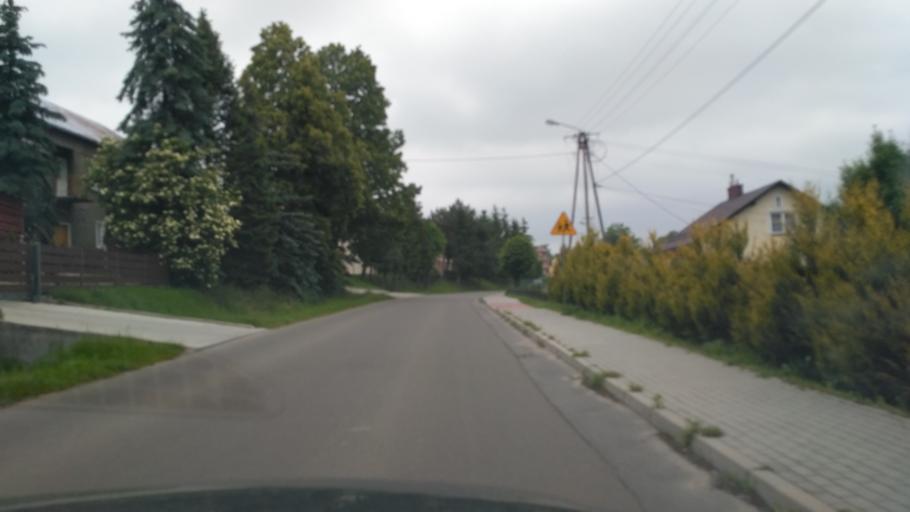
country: PL
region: Subcarpathian Voivodeship
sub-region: Powiat ropczycko-sedziszowski
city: Zagorzyce
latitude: 50.0325
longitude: 21.6874
